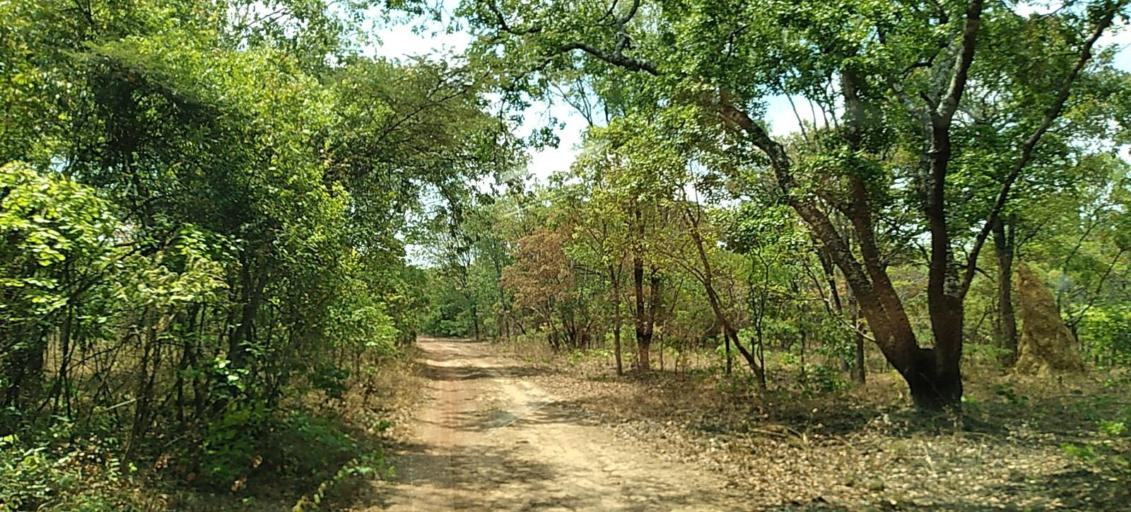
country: ZM
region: Copperbelt
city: Chililabombwe
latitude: -12.4620
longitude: 27.6465
